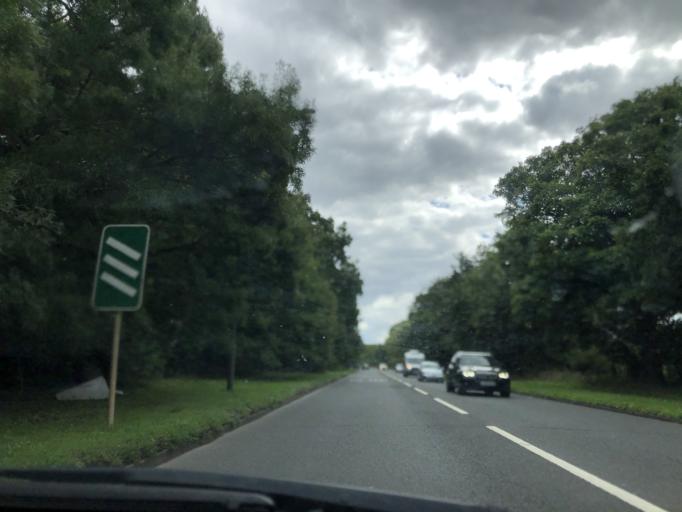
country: GB
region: England
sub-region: Kent
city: Halstead
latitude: 51.3486
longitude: 0.1325
